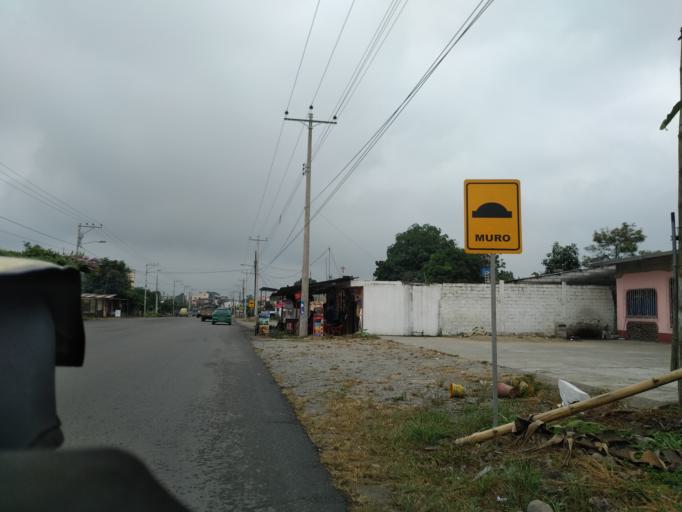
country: EC
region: Cotopaxi
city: La Mana
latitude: -0.9452
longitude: -79.3315
